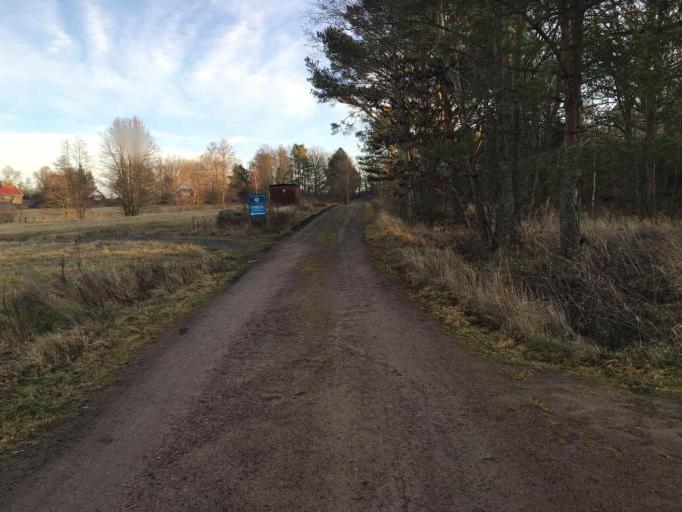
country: SE
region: Kalmar
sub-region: Vasterviks Kommun
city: Vaestervik
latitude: 57.6264
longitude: 16.5291
